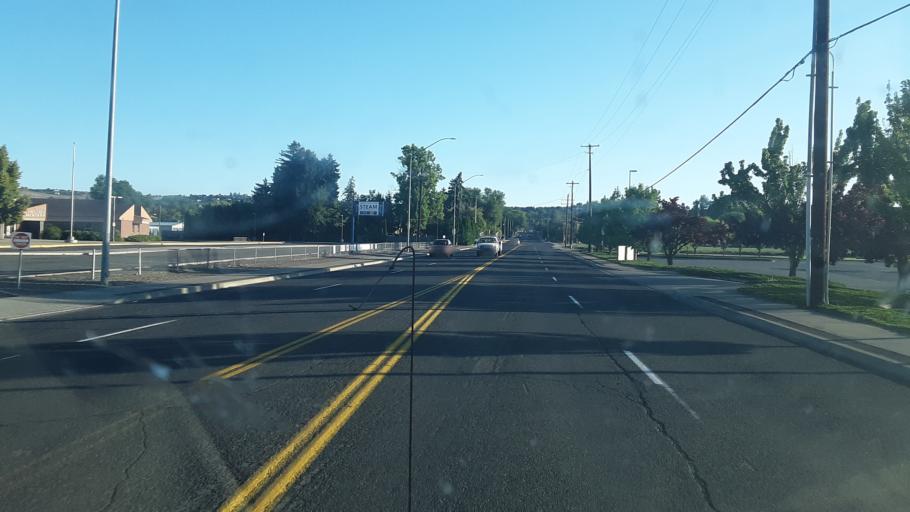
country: US
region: Washington
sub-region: Yakima County
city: West Valley
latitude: 46.5862
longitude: -120.6043
